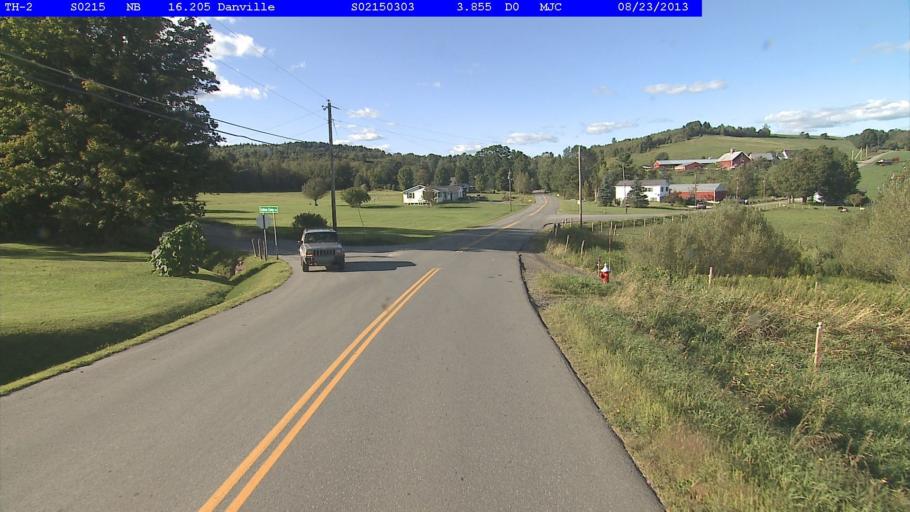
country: US
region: Vermont
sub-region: Caledonia County
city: Saint Johnsbury
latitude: 44.4196
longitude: -72.1423
